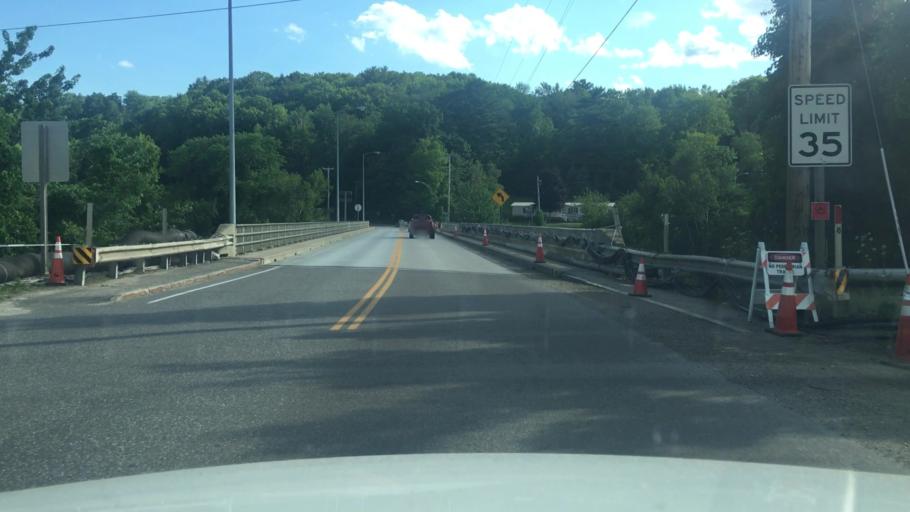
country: US
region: Maine
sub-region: Androscoggin County
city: Livermore Falls
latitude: 44.4733
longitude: -70.1915
